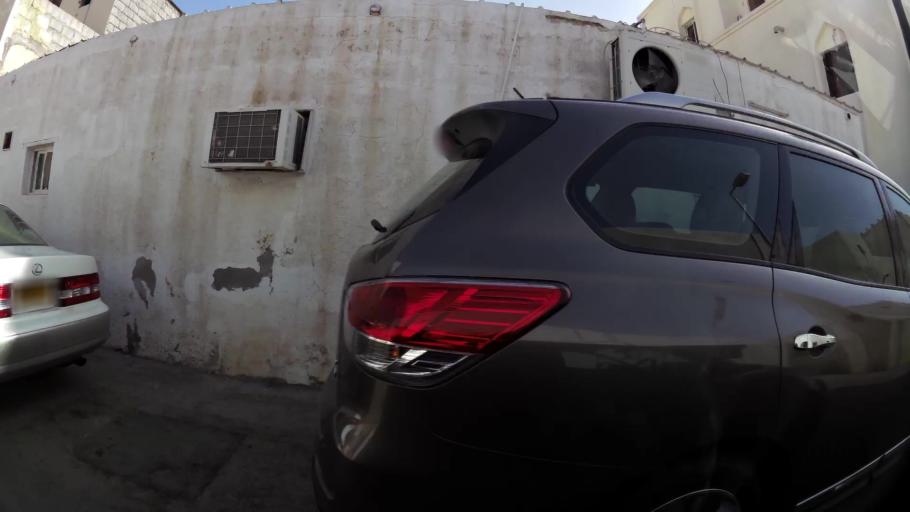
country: OM
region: Muhafazat Masqat
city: Muscat
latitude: 23.5839
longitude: 58.5190
